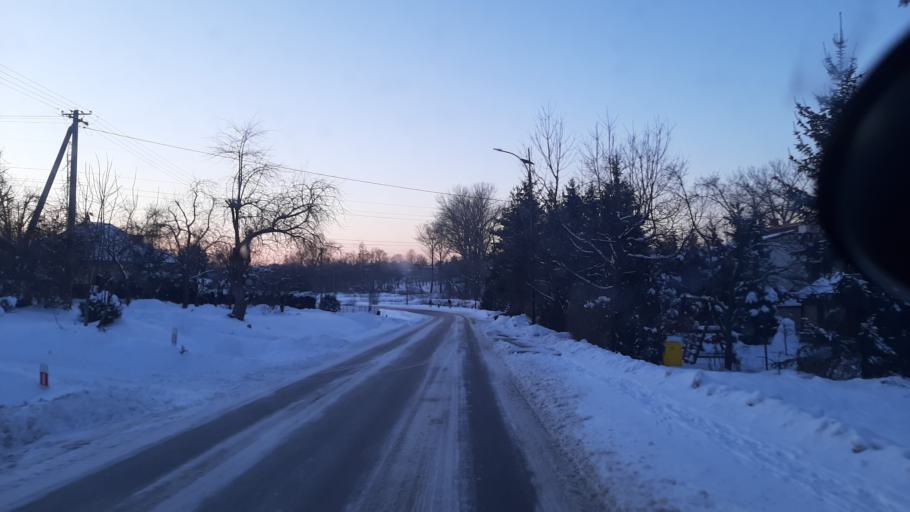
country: PL
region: Lublin Voivodeship
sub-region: Powiat lubelski
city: Jakubowice Murowane
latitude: 51.3163
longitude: 22.5994
